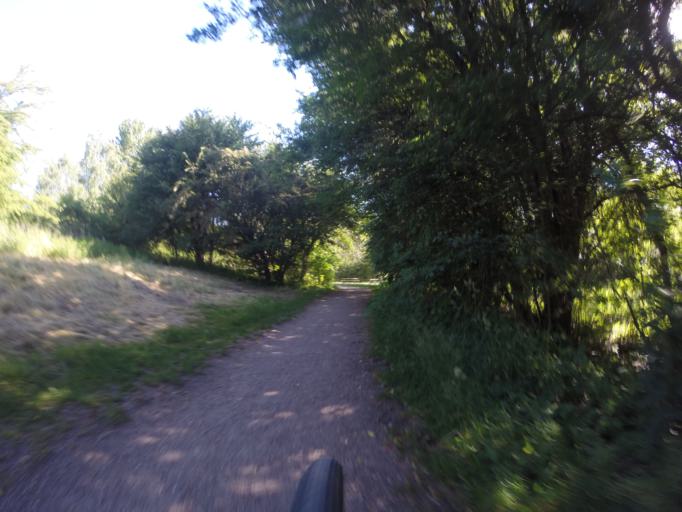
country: DK
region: Capital Region
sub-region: Herlev Kommune
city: Herlev
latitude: 55.7520
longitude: 12.4405
